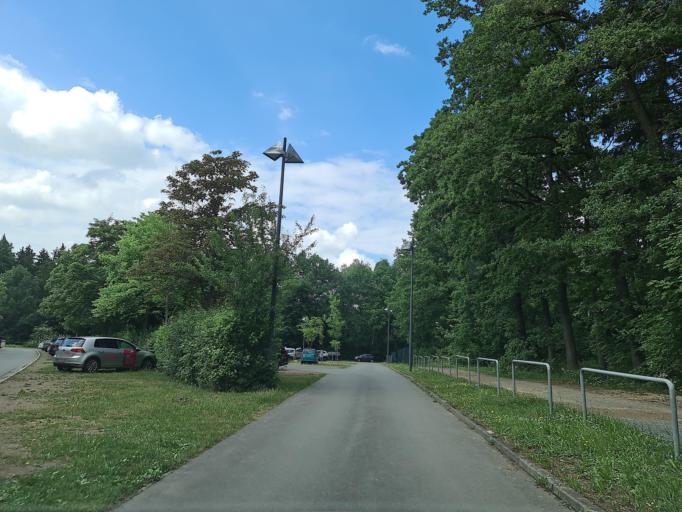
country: DE
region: Saxony
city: Pohl
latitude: 50.5404
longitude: 12.1852
